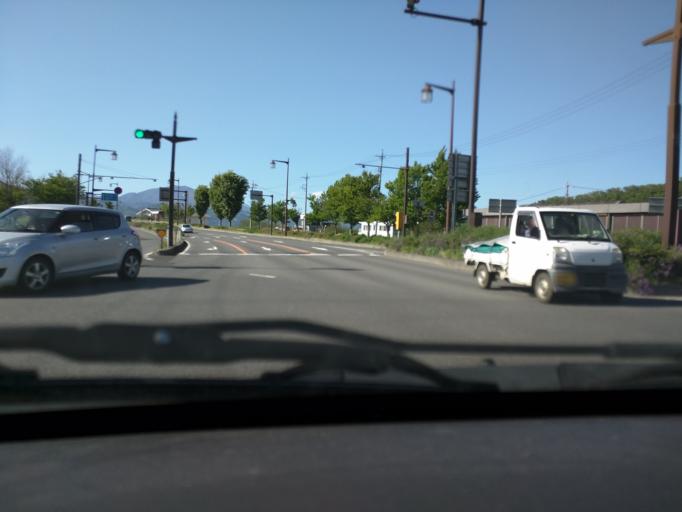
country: JP
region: Nagano
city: Nagano-shi
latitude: 36.5774
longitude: 138.1976
